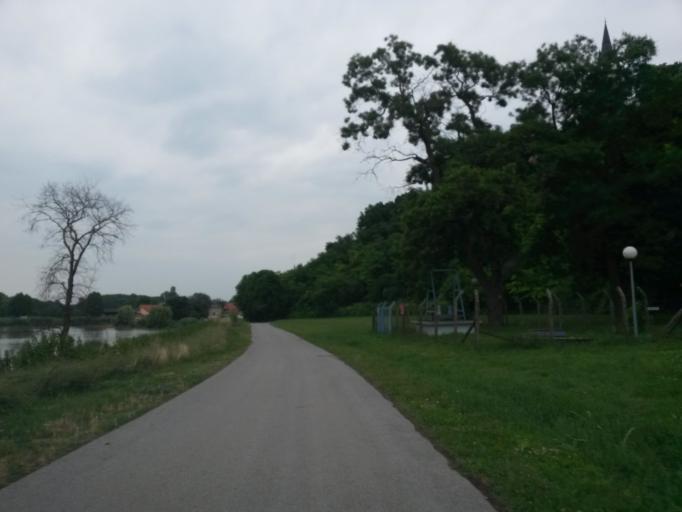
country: HR
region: Vukovarsko-Srijemska
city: Ilok
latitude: 45.2255
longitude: 19.3753
